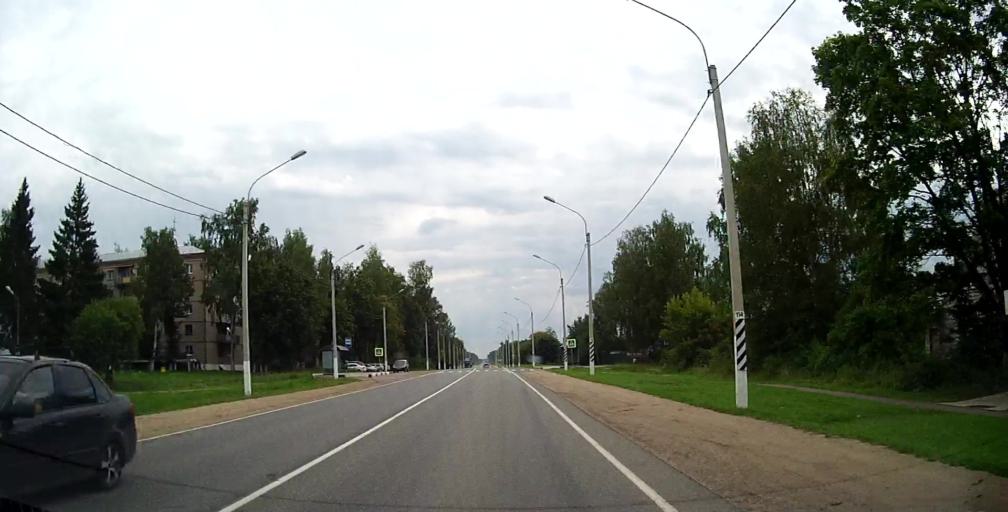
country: RU
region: Smolensk
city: Katyn'
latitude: 54.7667
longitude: 31.7419
